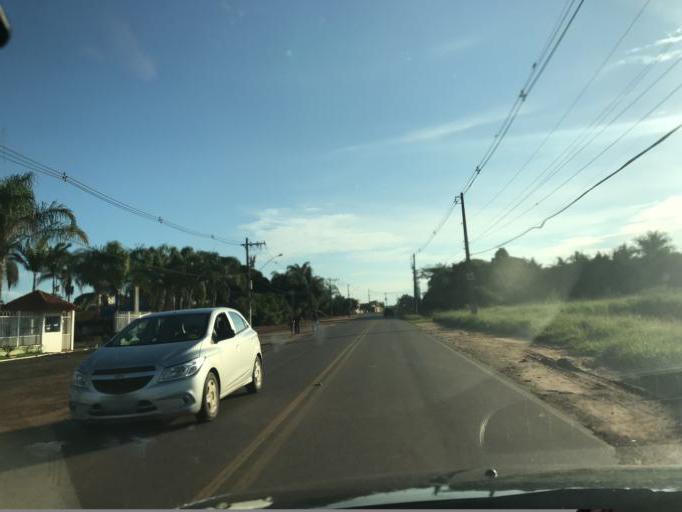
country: BR
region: Minas Gerais
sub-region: Tres Coracoes
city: Tres Coracoes
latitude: -21.6883
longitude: -45.2354
